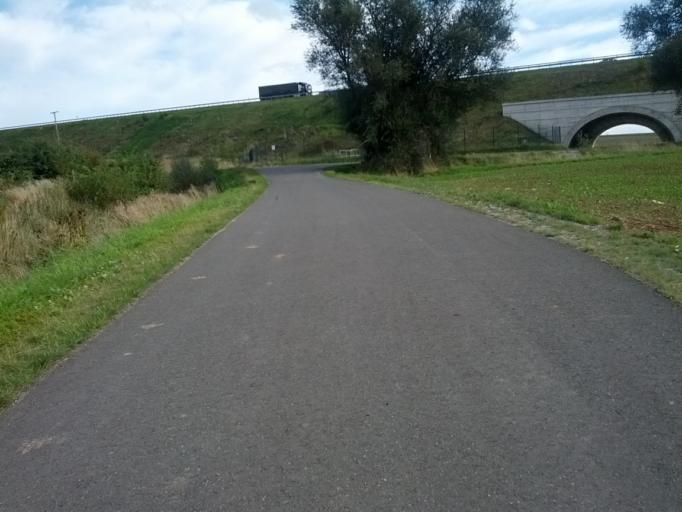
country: DE
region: Thuringia
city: Eisenach
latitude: 51.0156
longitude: 10.3072
